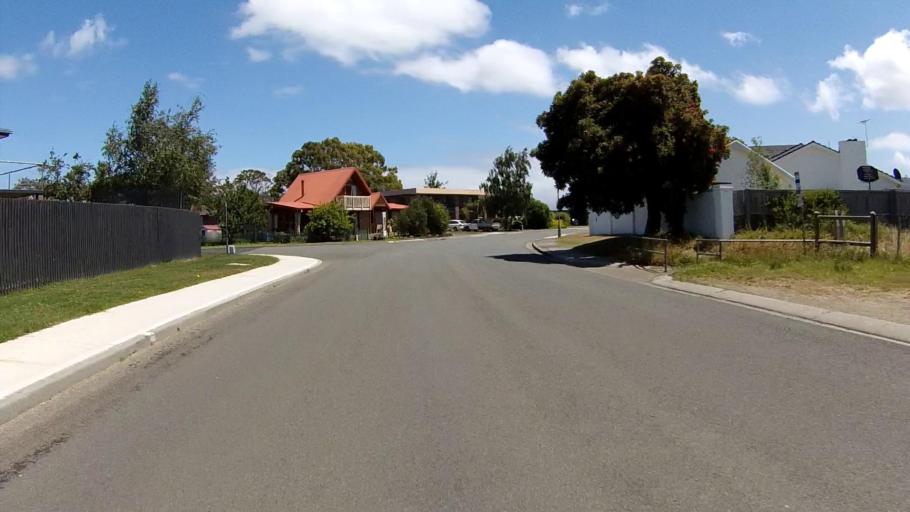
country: AU
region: Tasmania
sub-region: Clarence
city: Lauderdale
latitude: -42.9177
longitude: 147.5009
